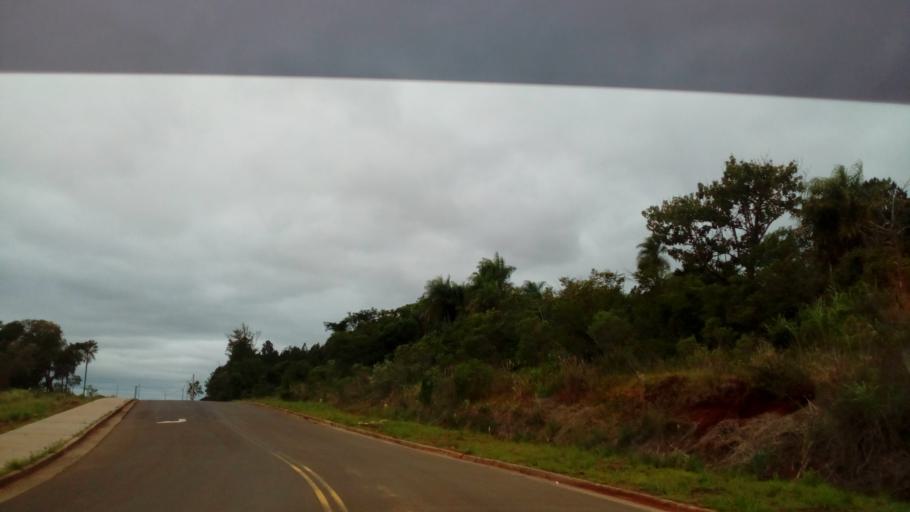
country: AR
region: Misiones
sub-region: Departamento de Candelaria
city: Candelaria
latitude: -27.4534
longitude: -55.7836
